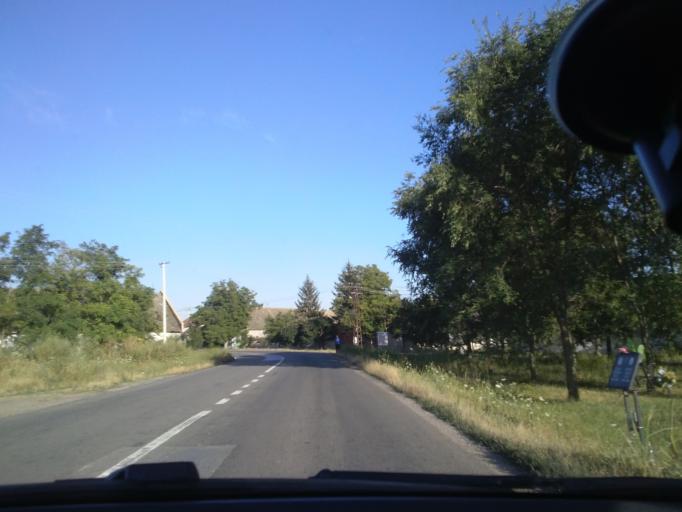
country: RS
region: Autonomna Pokrajina Vojvodina
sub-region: Zapadnobacki Okrug
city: Odzaci
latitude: 45.4585
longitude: 19.3240
